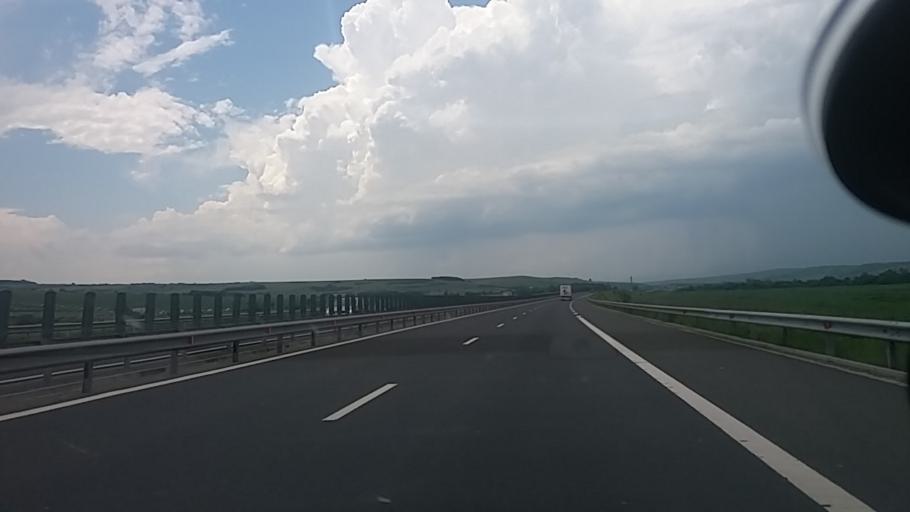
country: RO
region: Alba
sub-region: Comuna Garbova
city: Garbova
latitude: 45.9020
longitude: 23.7568
